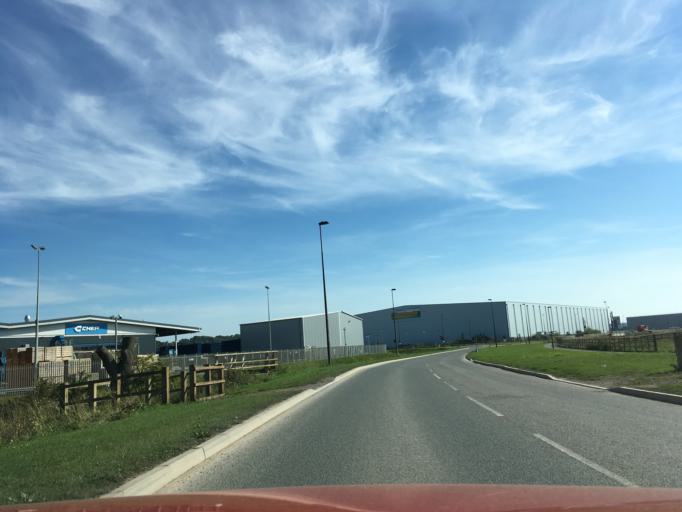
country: GB
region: England
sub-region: South Gloucestershire
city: Severn Beach
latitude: 51.5464
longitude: -2.6445
